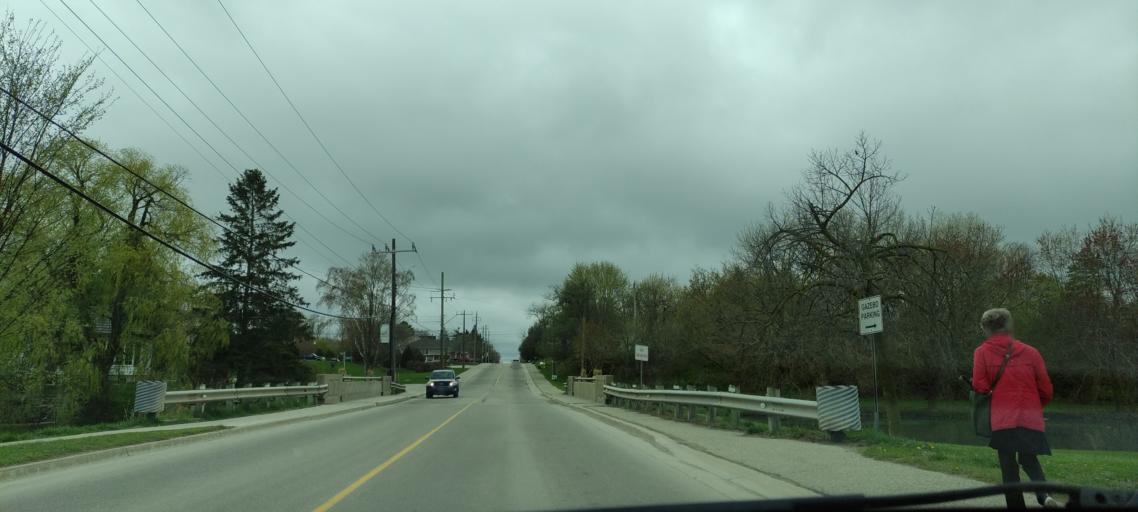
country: CA
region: Ontario
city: Stratford
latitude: 43.4778
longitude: -80.7680
